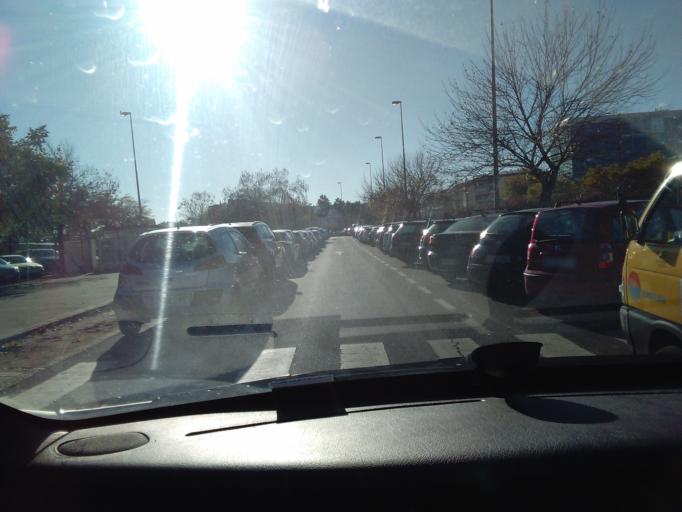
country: ES
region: Andalusia
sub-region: Provincia de Sevilla
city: Sevilla
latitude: 37.3928
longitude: -5.9762
